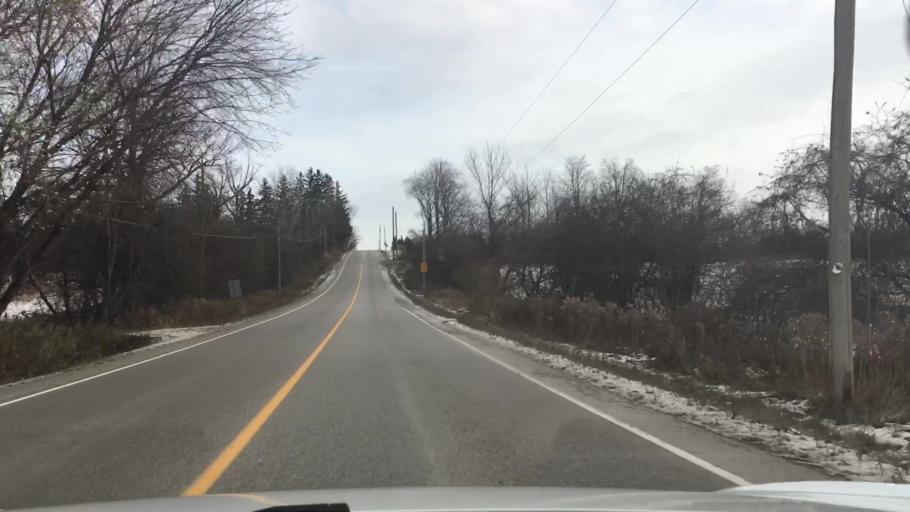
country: CA
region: Ontario
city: Oshawa
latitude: 43.9802
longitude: -78.8428
